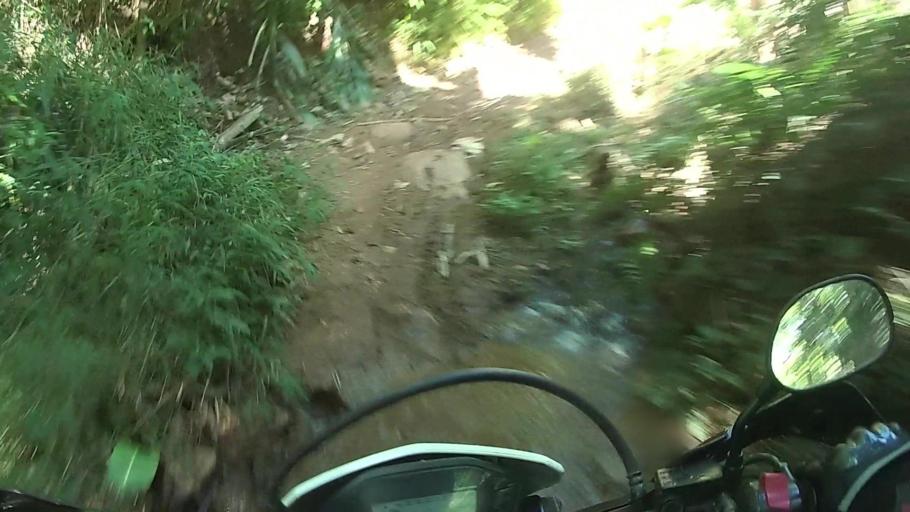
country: TH
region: Chiang Mai
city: Phrao
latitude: 19.5030
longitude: 99.2936
